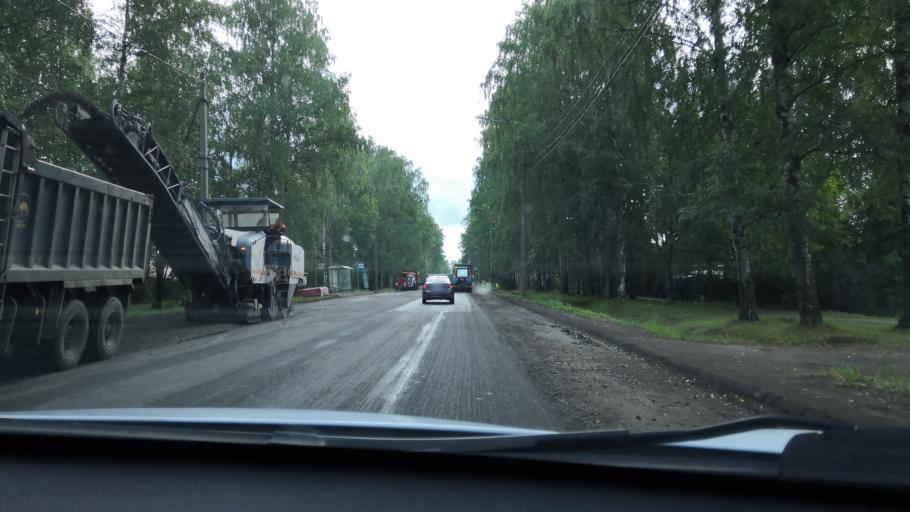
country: RU
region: St.-Petersburg
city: Tyarlevo
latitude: 59.7122
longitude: 30.4442
